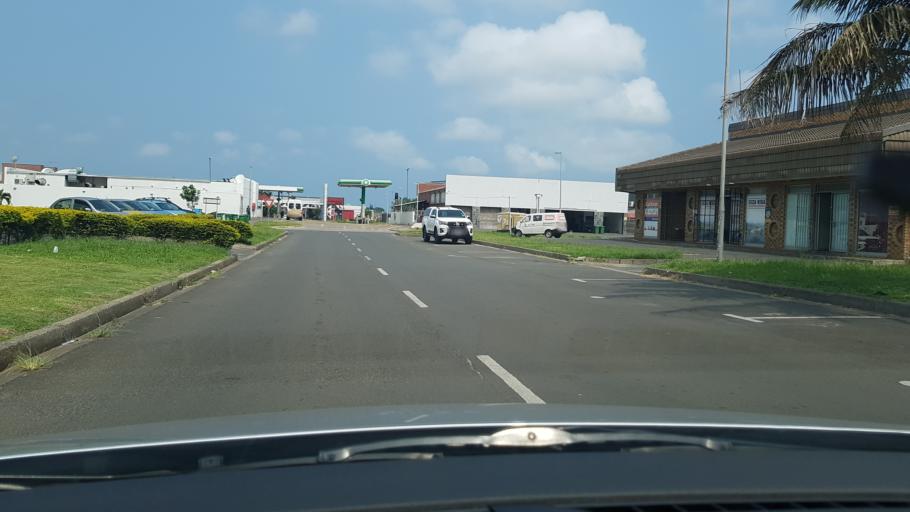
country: ZA
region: KwaZulu-Natal
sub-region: uThungulu District Municipality
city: Richards Bay
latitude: -28.7464
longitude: 32.0483
